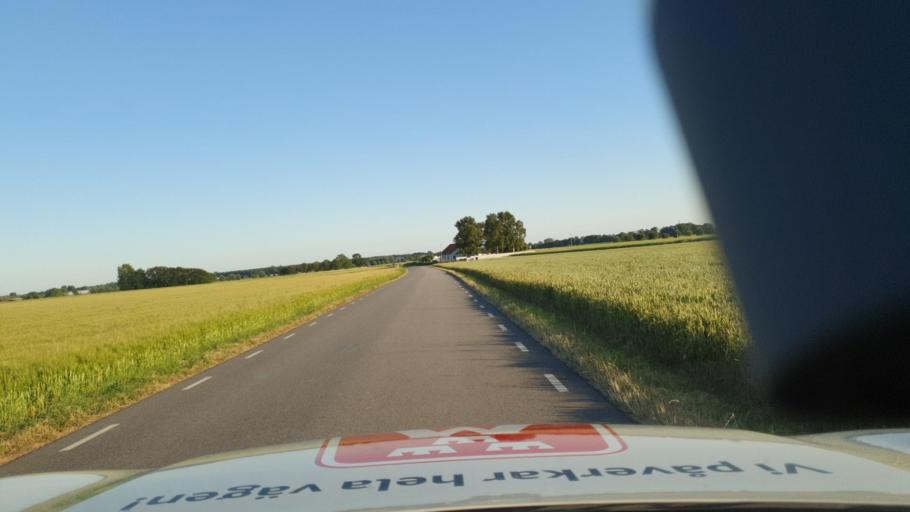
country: SE
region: Skane
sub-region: Lomma Kommun
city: Lomma
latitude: 55.7121
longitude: 13.0593
